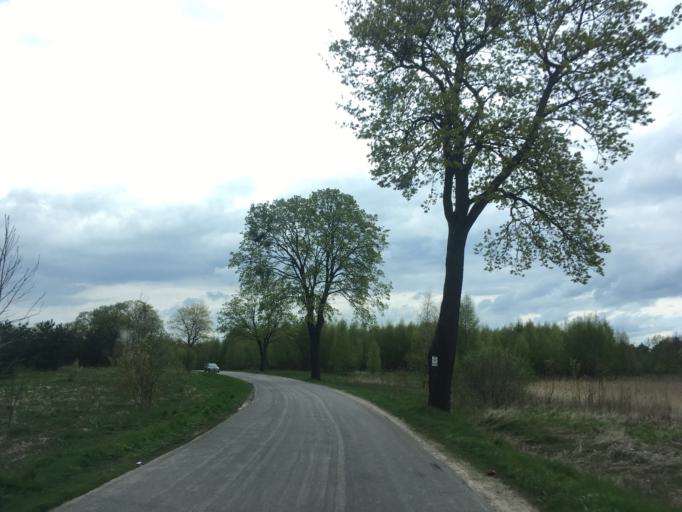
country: PL
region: Warmian-Masurian Voivodeship
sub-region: Powiat nidzicki
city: Kozlowo
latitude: 53.4102
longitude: 20.2727
